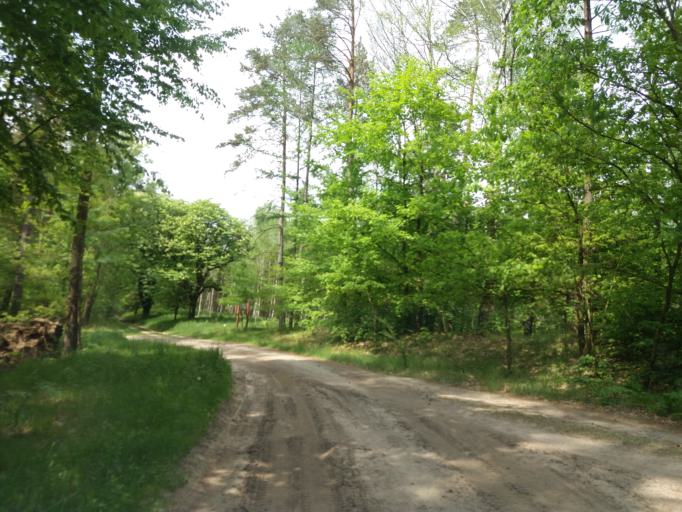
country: PL
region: West Pomeranian Voivodeship
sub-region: Powiat choszczenski
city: Drawno
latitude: 53.1942
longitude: 15.7643
